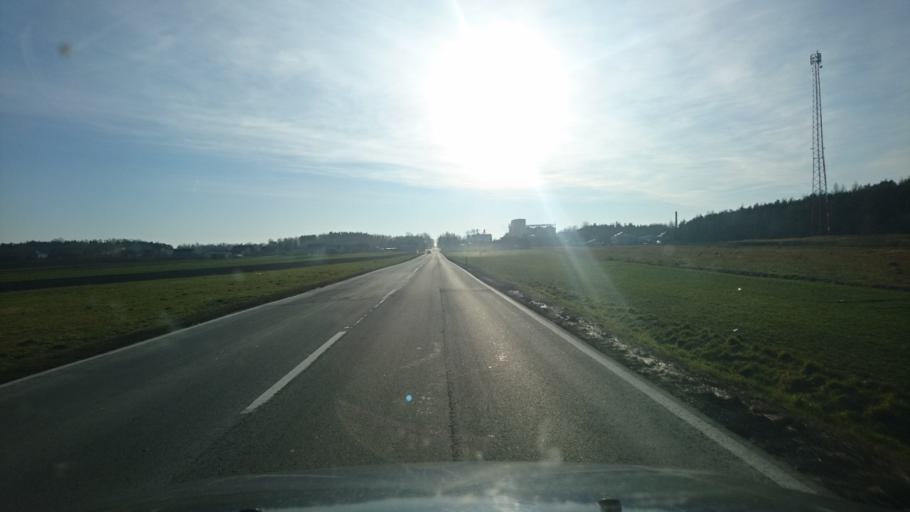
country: PL
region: Opole Voivodeship
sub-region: Powiat oleski
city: Dalachow
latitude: 51.0797
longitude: 18.6035
